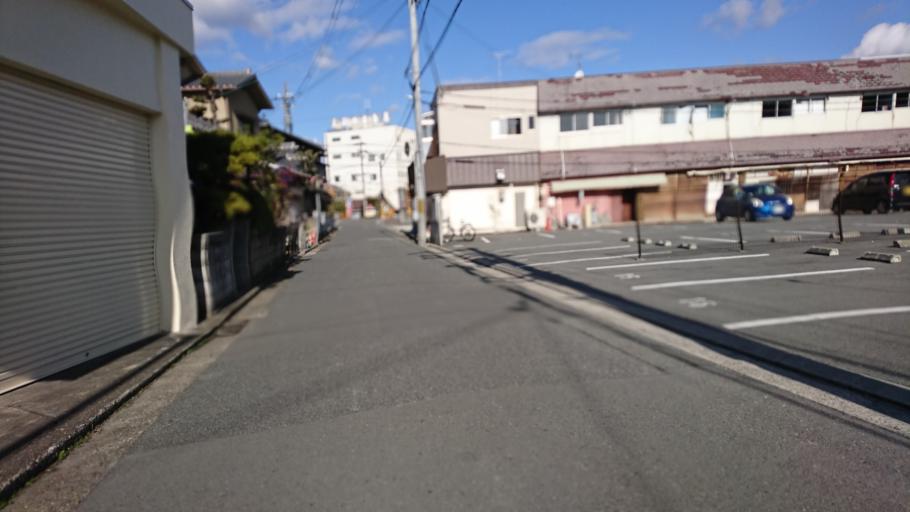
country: JP
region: Hyogo
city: Kakogawacho-honmachi
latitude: 34.7749
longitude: 134.7728
